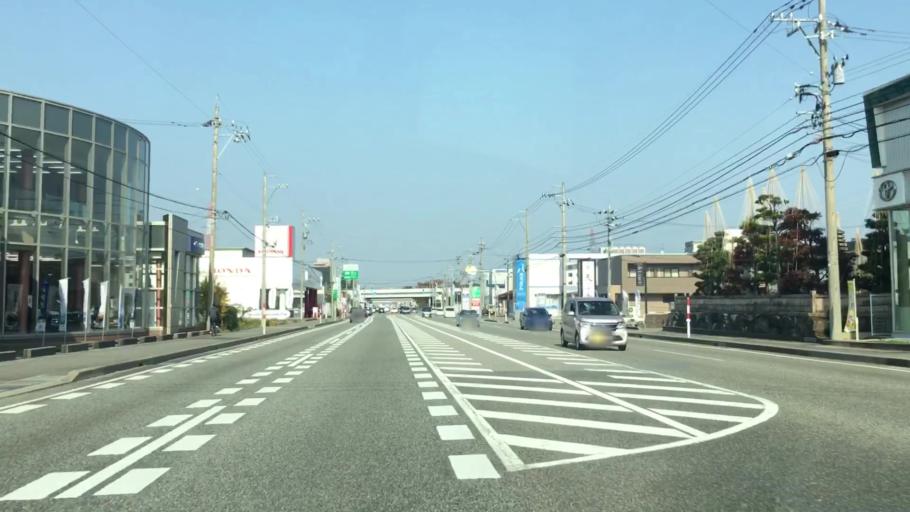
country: JP
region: Toyama
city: Toyama-shi
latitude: 36.6498
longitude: 137.2096
